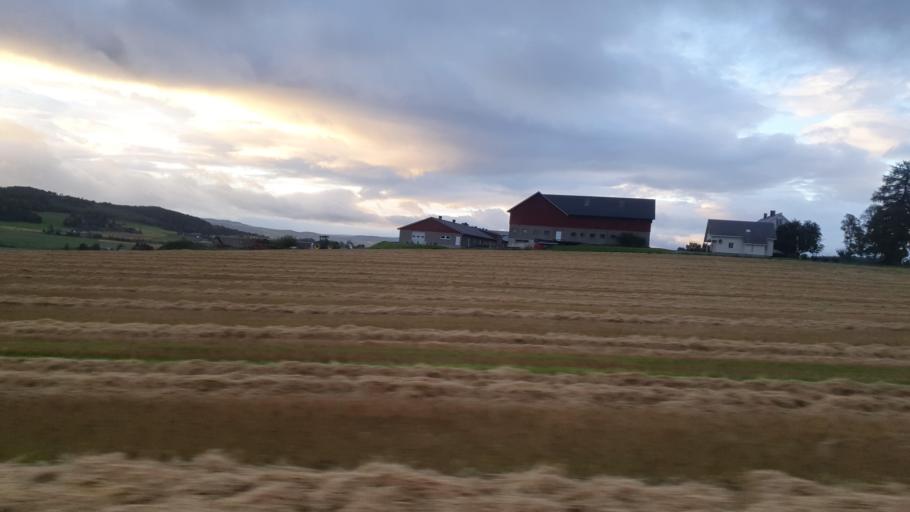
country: NO
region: Nord-Trondelag
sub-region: Levanger
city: Skogn
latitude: 63.6814
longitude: 11.1716
